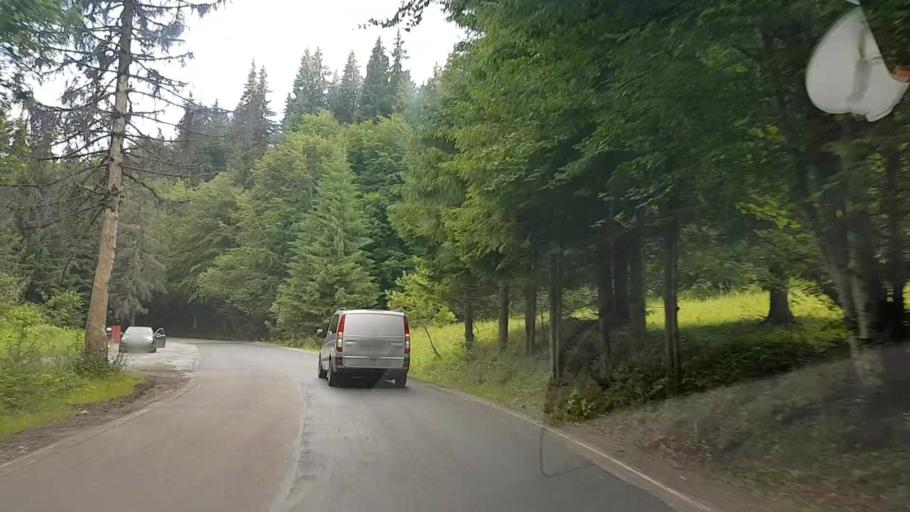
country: RO
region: Harghita
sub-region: Comuna Varsag
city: Varsag
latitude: 46.6649
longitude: 25.3187
